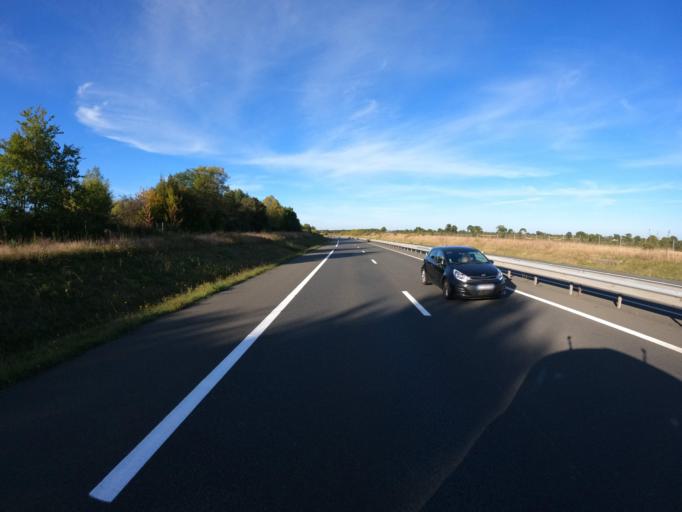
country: FR
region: Pays de la Loire
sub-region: Departement de Maine-et-Loire
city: Saint-Lambert-du-Lattay
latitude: 47.2609
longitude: -0.6160
